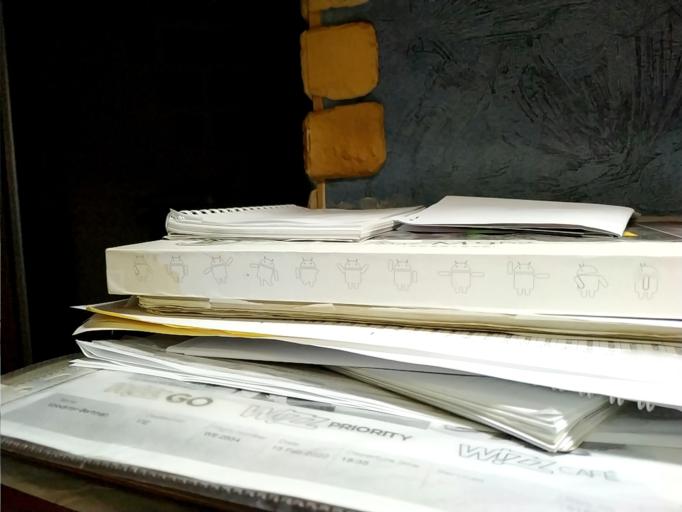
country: RU
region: Arkhangelskaya
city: Onega
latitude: 63.4751
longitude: 38.1603
